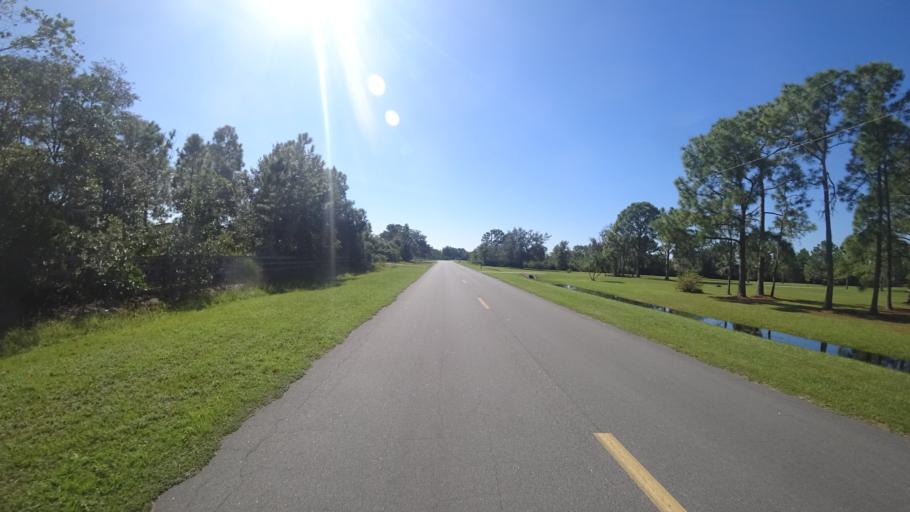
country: US
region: Florida
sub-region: Sarasota County
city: Lake Sarasota
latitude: 27.3609
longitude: -82.2508
